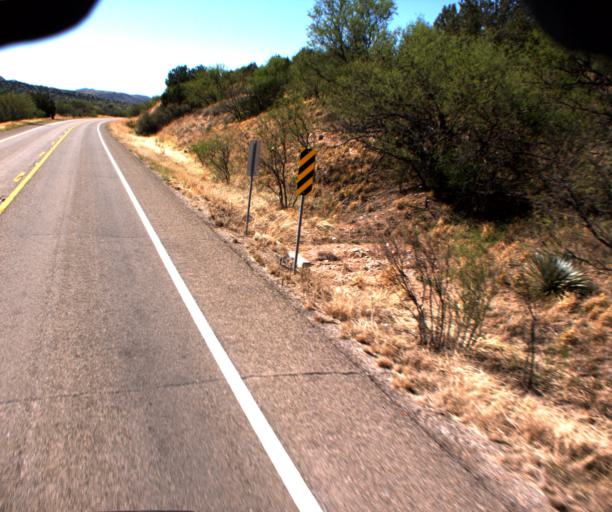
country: US
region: Arizona
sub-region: Santa Cruz County
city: Rio Rico
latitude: 31.6384
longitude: -110.7137
